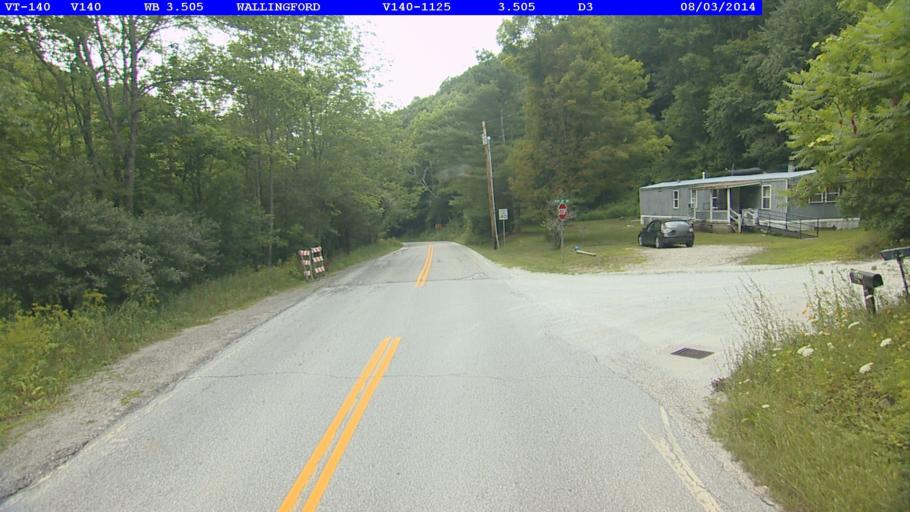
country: US
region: Vermont
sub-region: Rutland County
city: Rutland
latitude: 43.4605
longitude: -72.9190
